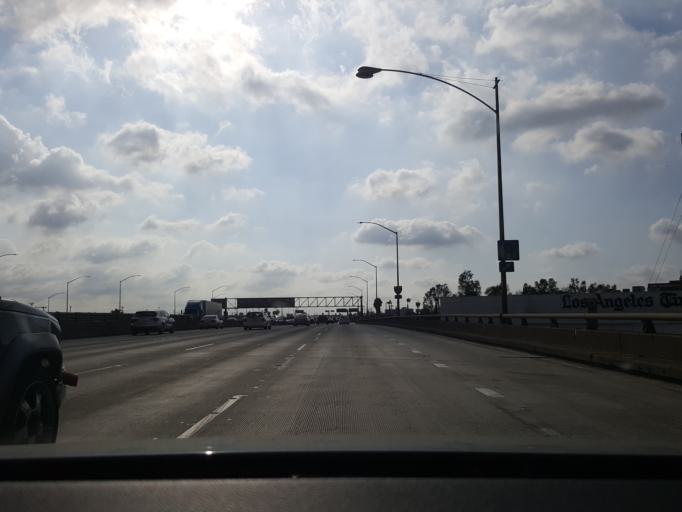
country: US
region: California
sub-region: Los Angeles County
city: Los Angeles
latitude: 34.0268
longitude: -118.2335
